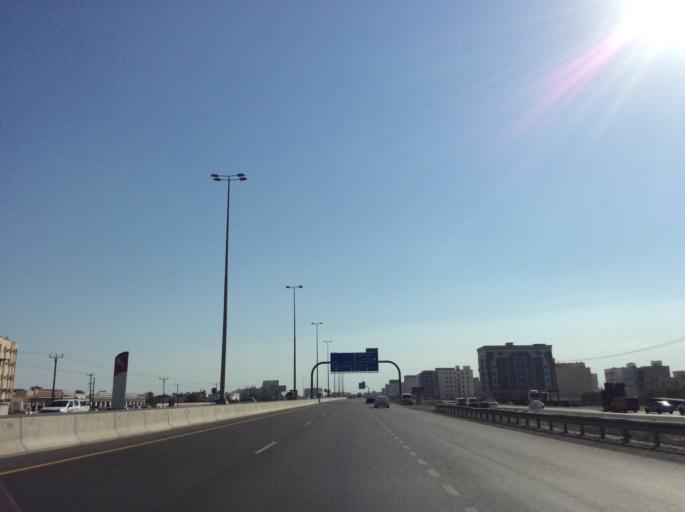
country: OM
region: Al Batinah
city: Al Liwa'
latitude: 24.4400
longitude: 56.6076
